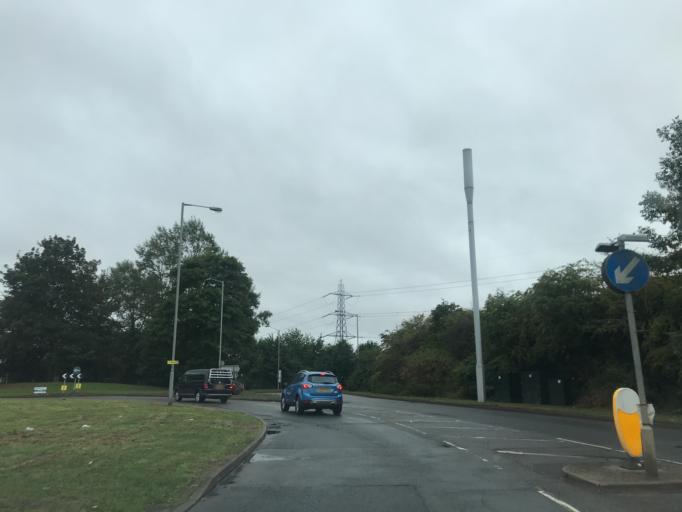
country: GB
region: England
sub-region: Buckinghamshire
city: Aylesbury
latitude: 51.8099
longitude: -0.8307
